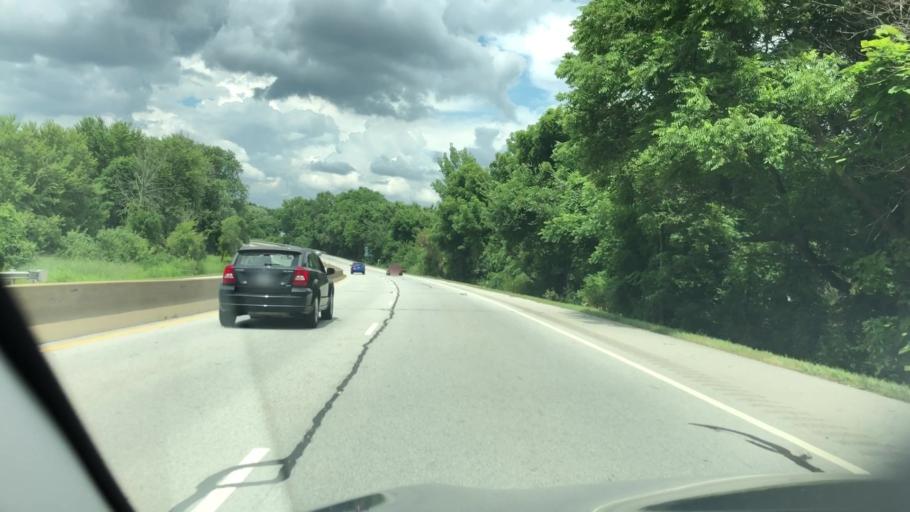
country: US
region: Ohio
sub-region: Stark County
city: Massillon
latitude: 40.8068
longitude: -81.5256
